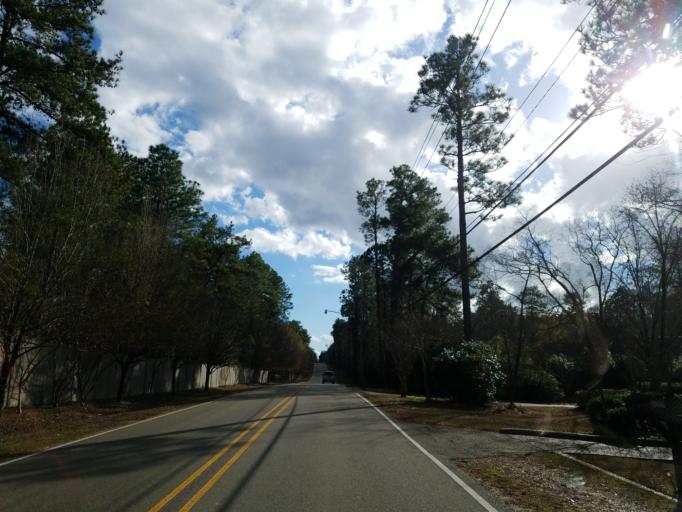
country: US
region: Mississippi
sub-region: Lamar County
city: West Hattiesburg
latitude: 31.3021
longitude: -89.3480
